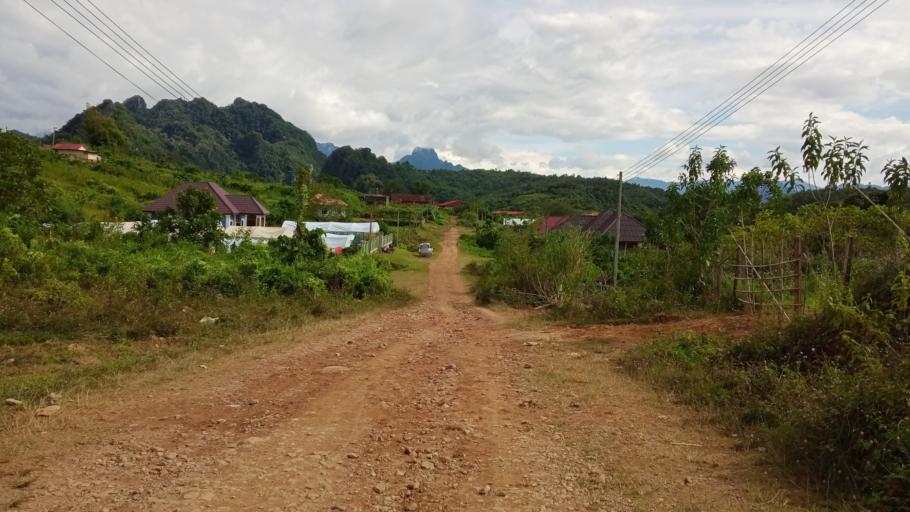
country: LA
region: Xiangkhoang
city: Phonsavan
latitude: 19.1071
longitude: 102.9275
